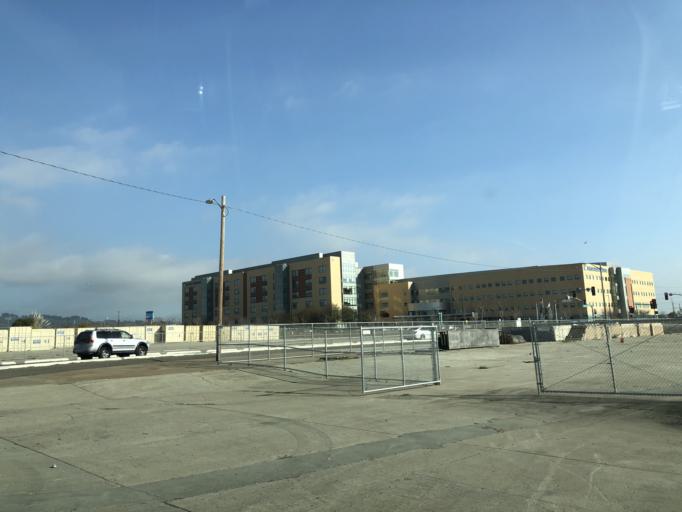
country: US
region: California
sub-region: Alameda County
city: San Leandro
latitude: 37.7073
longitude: -122.1682
